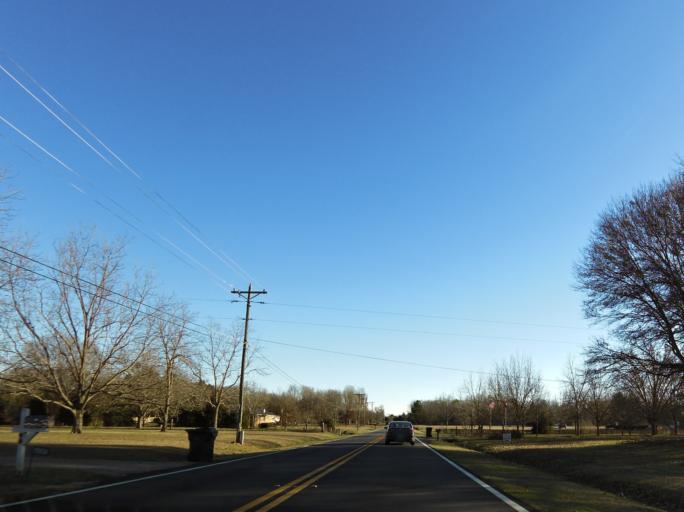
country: US
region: Georgia
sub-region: Houston County
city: Centerville
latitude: 32.6546
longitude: -83.6967
